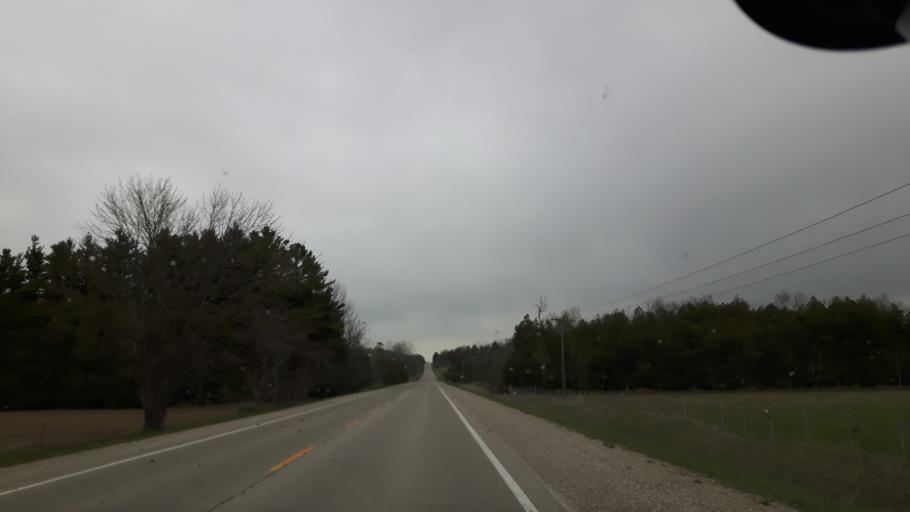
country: CA
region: Ontario
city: Bluewater
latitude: 43.5894
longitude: -81.5884
